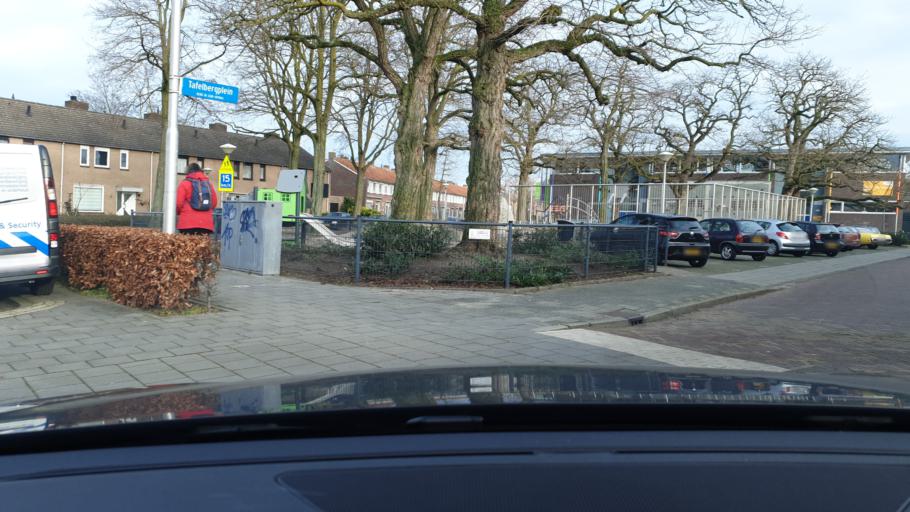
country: NL
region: North Brabant
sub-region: Gemeente Eindhoven
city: De Doornakkers
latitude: 51.4409
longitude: 5.5085
